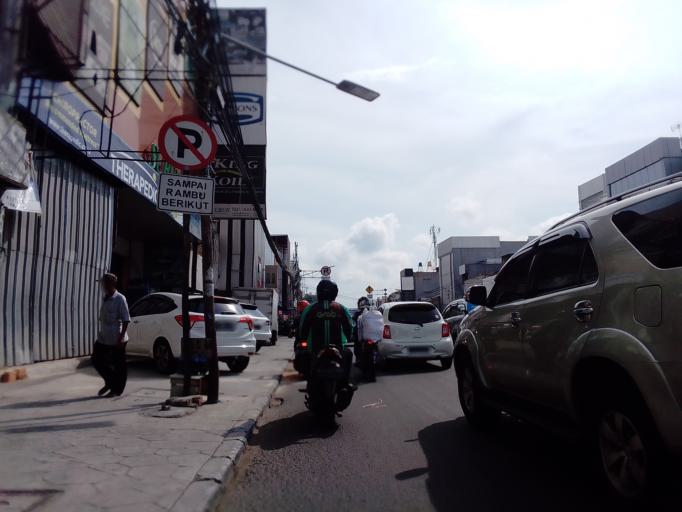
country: ID
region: Jakarta Raya
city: Jakarta
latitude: -6.1659
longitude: 106.8072
